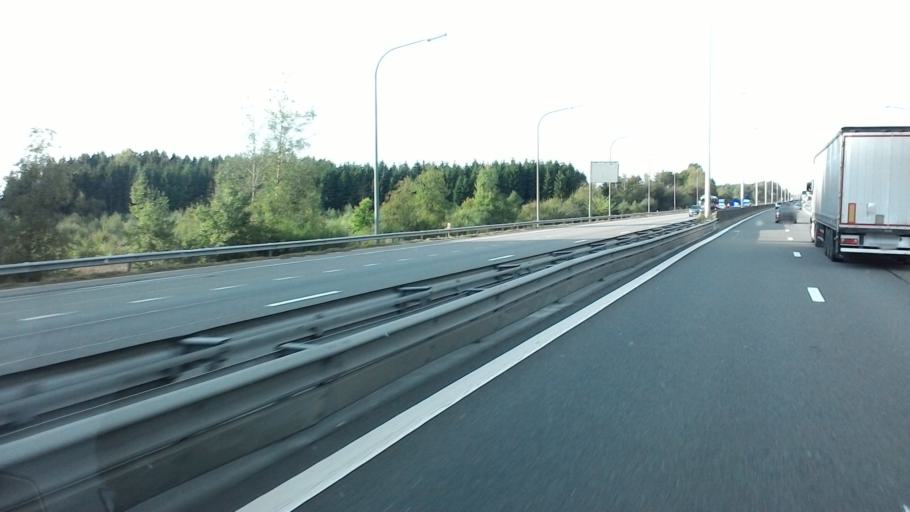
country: BE
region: Wallonia
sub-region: Province du Luxembourg
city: Leglise
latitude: 49.8119
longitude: 5.5163
